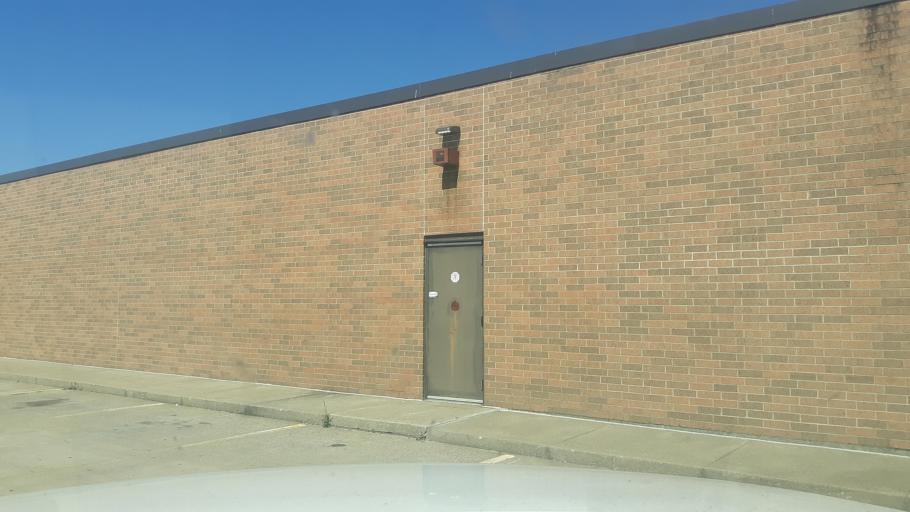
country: US
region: Illinois
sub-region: Saline County
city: Harrisburg
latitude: 37.7445
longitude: -88.5232
